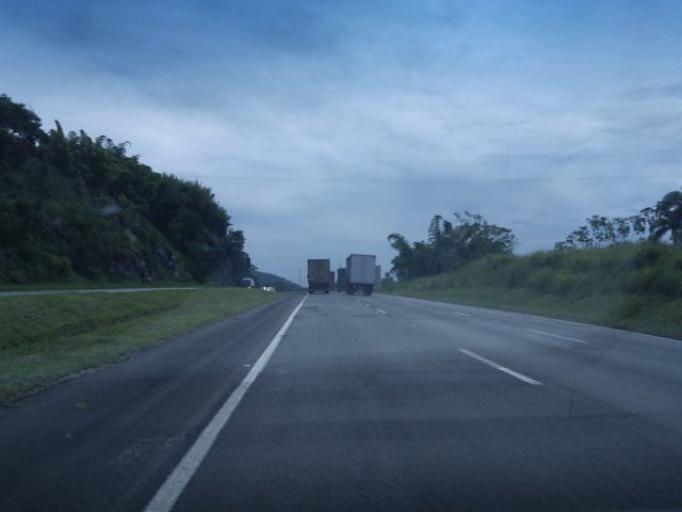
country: BR
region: Sao Paulo
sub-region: Miracatu
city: Miracatu
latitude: -24.3156
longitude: -47.5247
